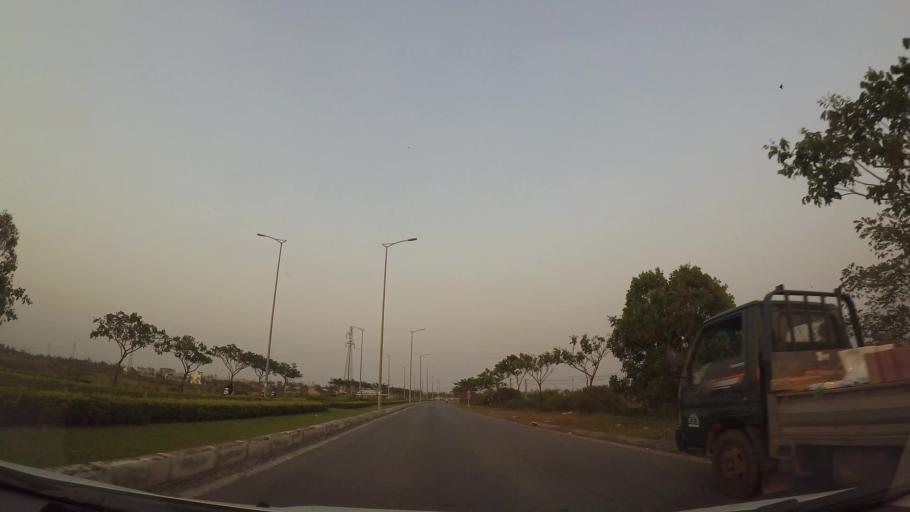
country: VN
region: Da Nang
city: Ngu Hanh Son
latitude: 15.9755
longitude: 108.2306
